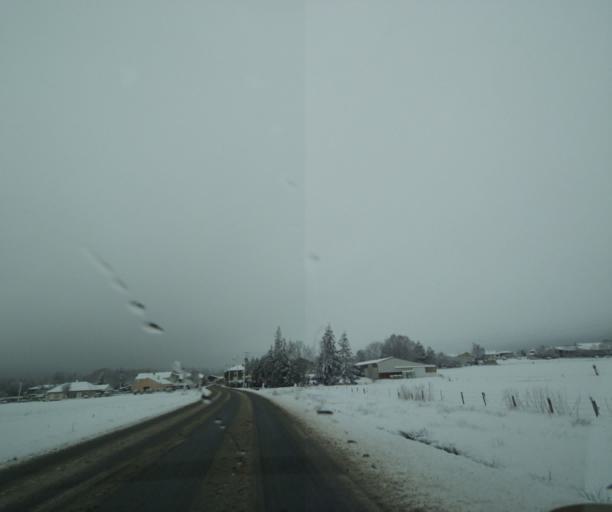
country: FR
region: Champagne-Ardenne
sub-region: Departement de la Haute-Marne
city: Wassy
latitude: 48.5225
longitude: 4.9323
